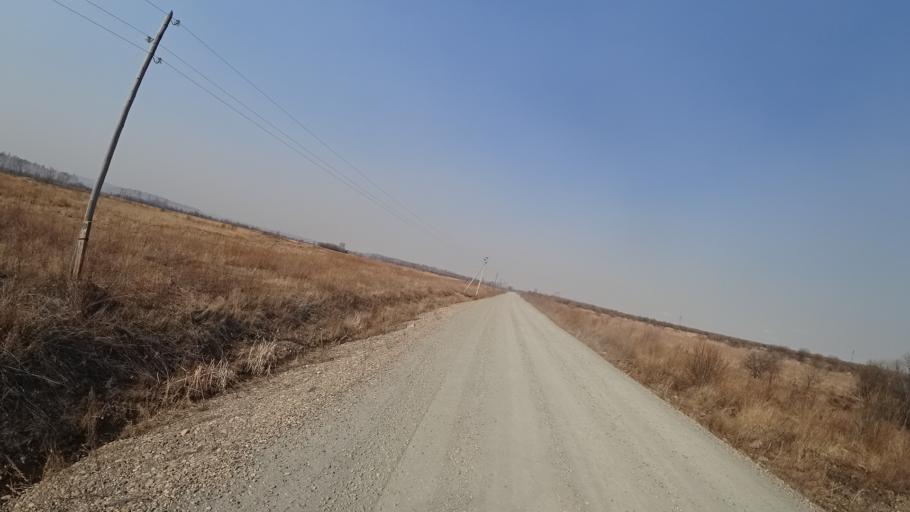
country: RU
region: Amur
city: Novobureyskiy
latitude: 49.8059
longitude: 129.9644
